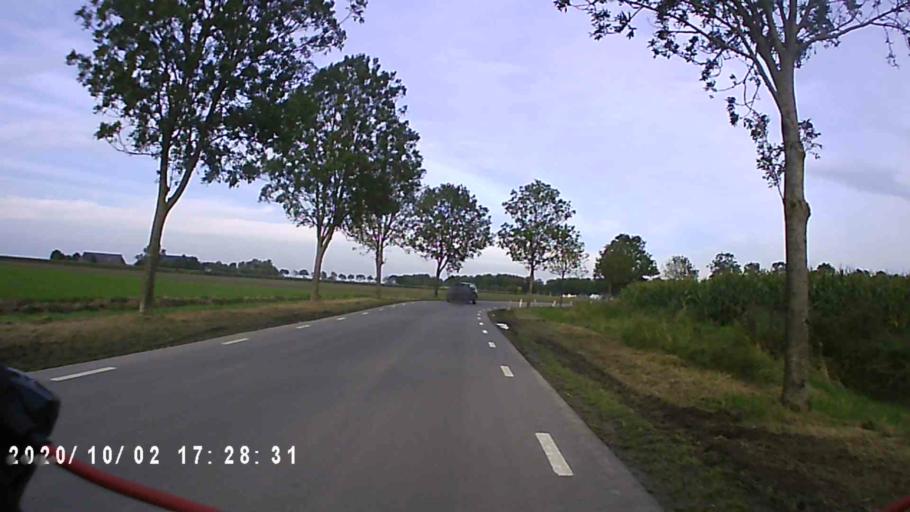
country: NL
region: Groningen
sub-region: Gemeente De Marne
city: Ulrum
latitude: 53.3370
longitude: 6.3166
